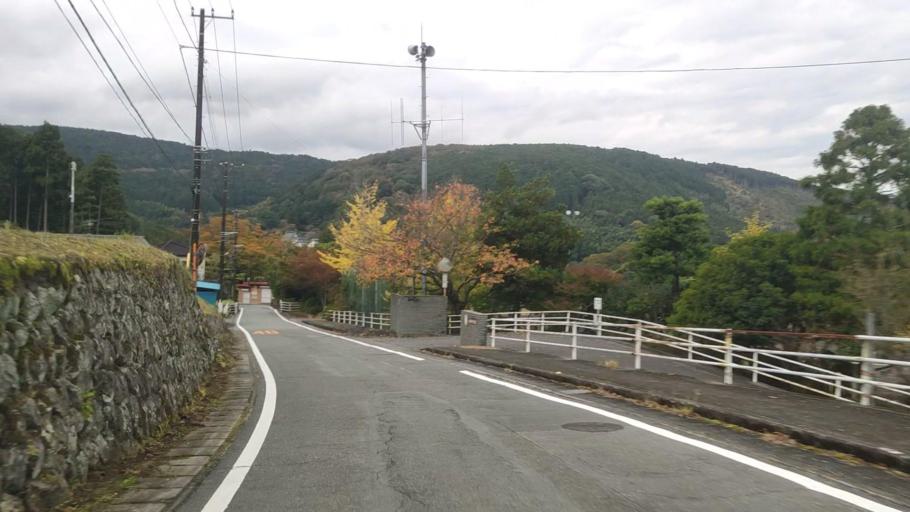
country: JP
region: Shizuoka
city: Ito
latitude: 34.9483
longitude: 139.0314
